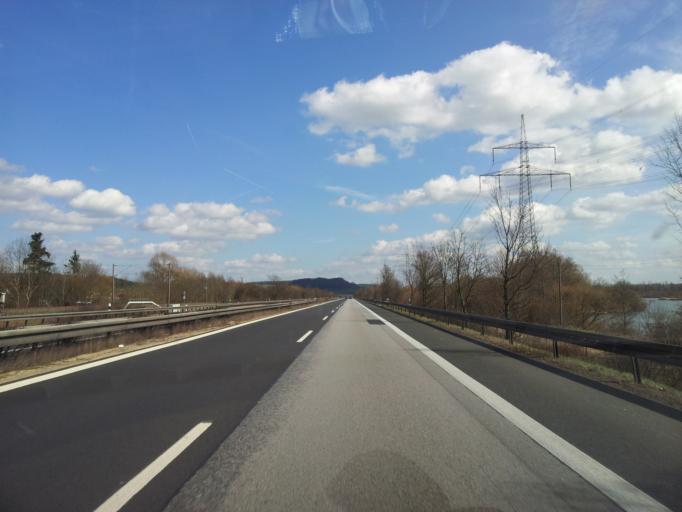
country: DE
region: Bavaria
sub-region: Regierungsbezirk Unterfranken
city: Stettfeld
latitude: 49.9732
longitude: 10.6986
